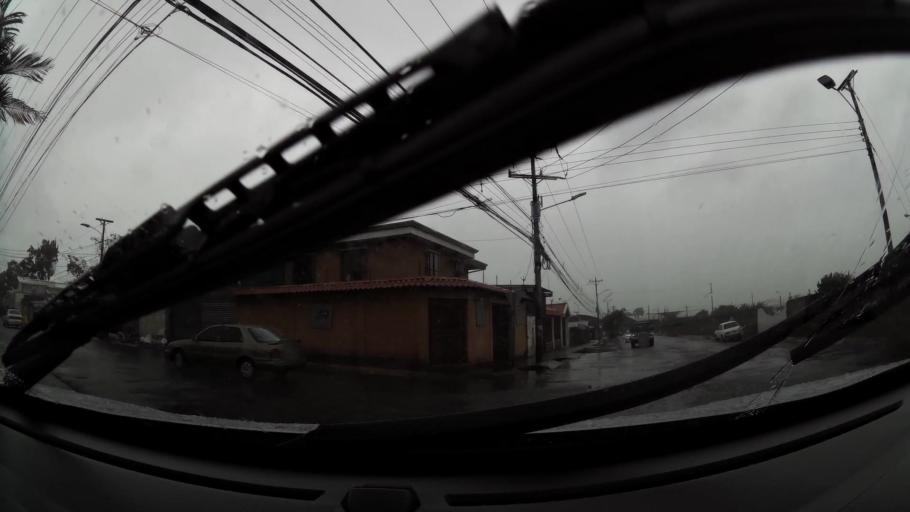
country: CR
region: Cartago
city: Cartago
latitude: 9.8647
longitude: -83.9326
